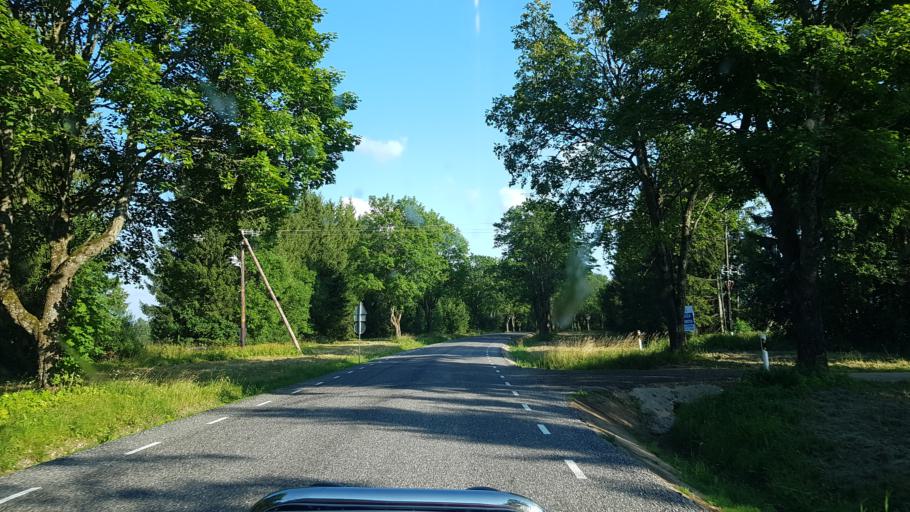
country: EE
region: Polvamaa
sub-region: Polva linn
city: Polva
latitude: 58.0115
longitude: 26.9246
